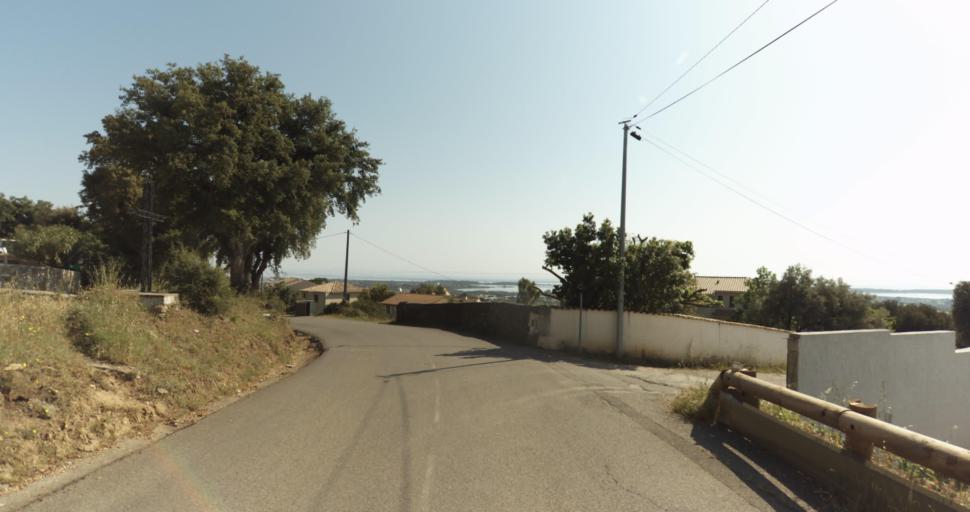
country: FR
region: Corsica
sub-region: Departement de la Haute-Corse
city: Biguglia
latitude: 42.6258
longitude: 9.4218
